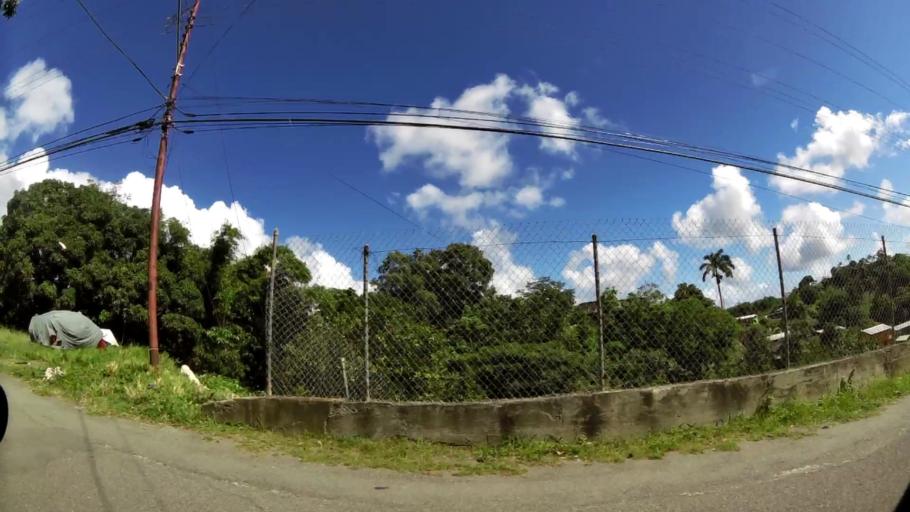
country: TT
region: Tobago
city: Scarborough
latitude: 11.2422
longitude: -60.7330
